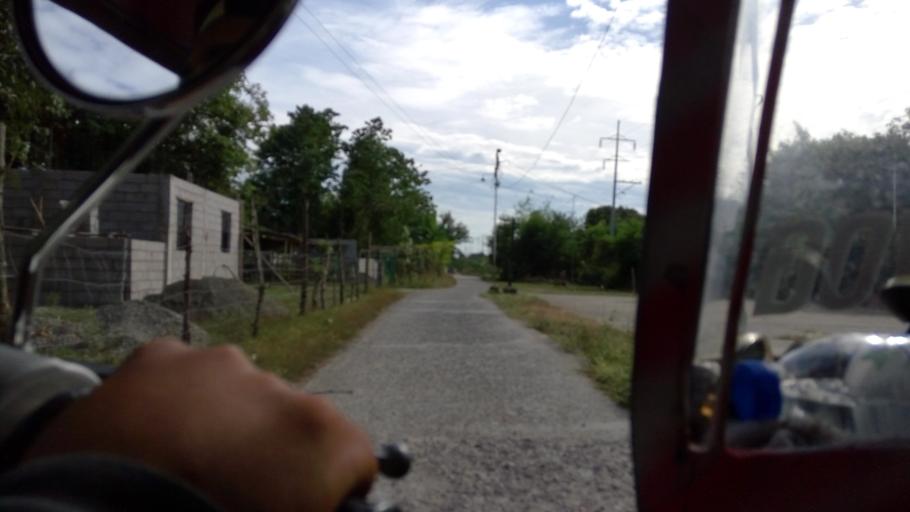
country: PH
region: Ilocos
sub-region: Province of La Union
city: San Eugenio
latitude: 16.3712
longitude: 120.3524
